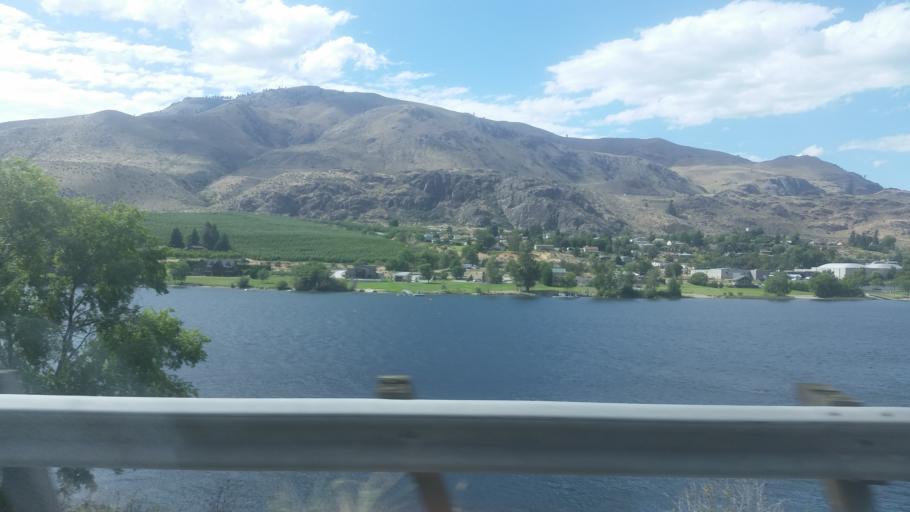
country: US
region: Washington
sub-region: Chelan County
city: Chelan
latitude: 47.7932
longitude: -119.9821
